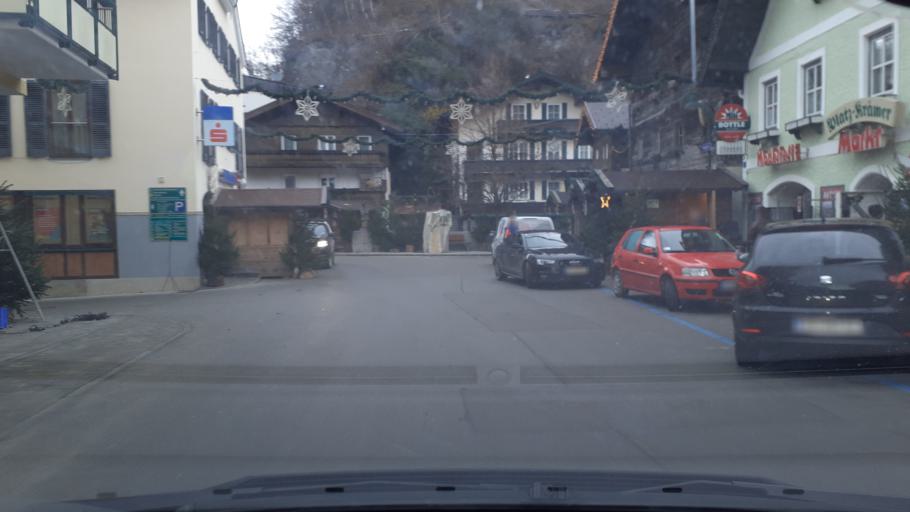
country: AT
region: Salzburg
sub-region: Politischer Bezirk Sankt Johann im Pongau
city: Huttschlag
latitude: 47.2373
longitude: 13.2014
